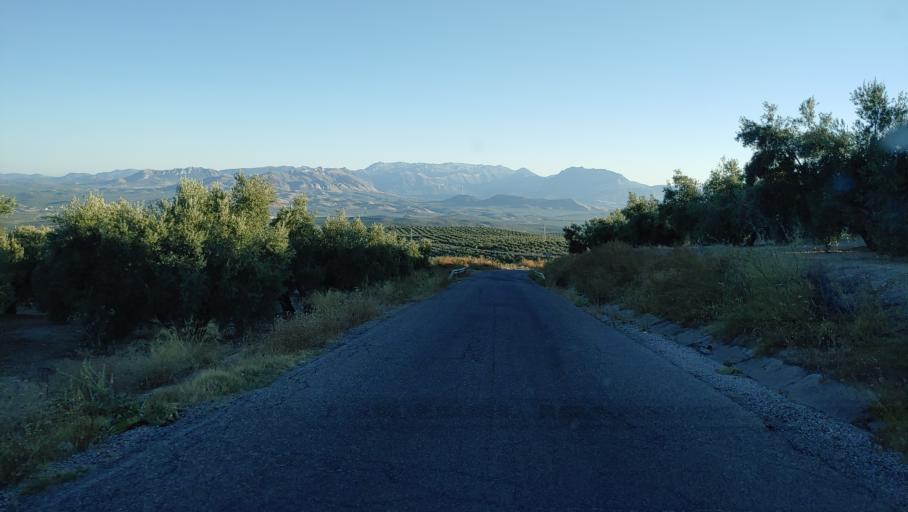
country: ES
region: Andalusia
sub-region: Provincia de Jaen
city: Ubeda
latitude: 37.9994
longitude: -3.3800
